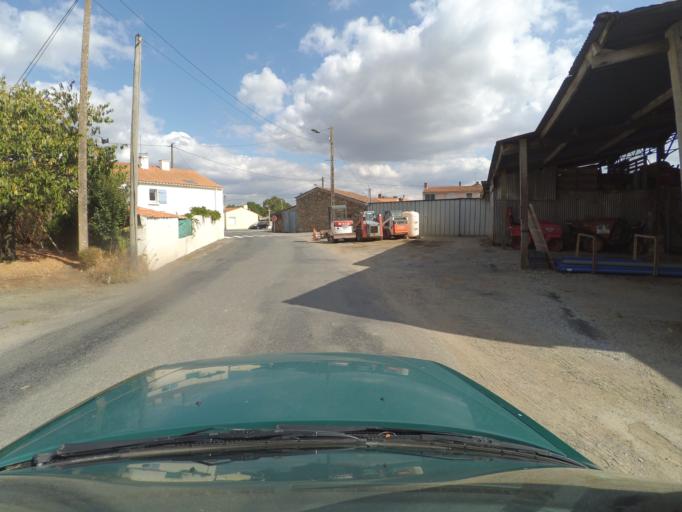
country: FR
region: Pays de la Loire
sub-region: Departement de la Loire-Atlantique
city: Vieillevigne
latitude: 46.9753
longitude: -1.4364
